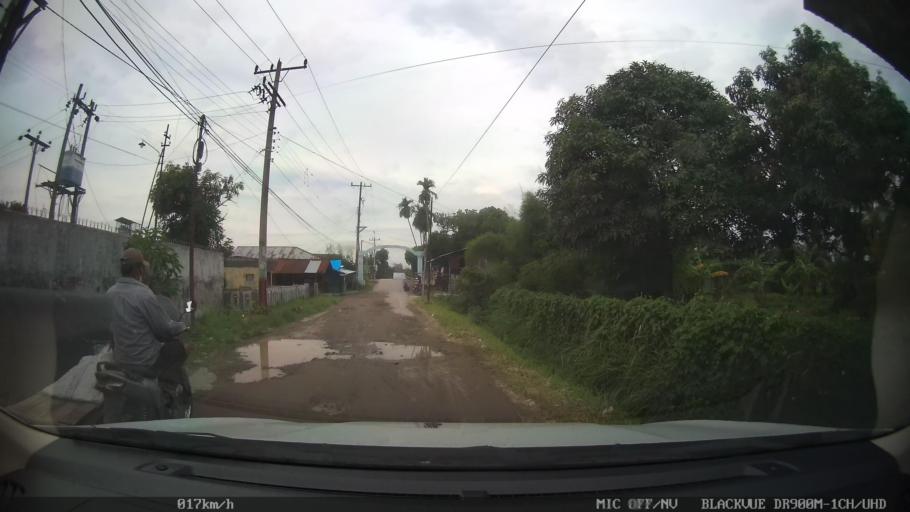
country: ID
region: North Sumatra
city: Sunggal
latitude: 3.6046
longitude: 98.6034
